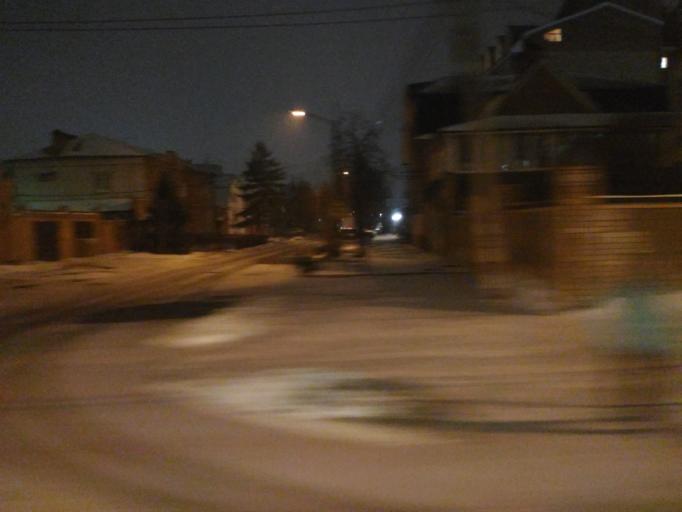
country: RU
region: Ulyanovsk
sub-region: Ulyanovskiy Rayon
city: Ulyanovsk
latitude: 54.3252
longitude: 48.4040
